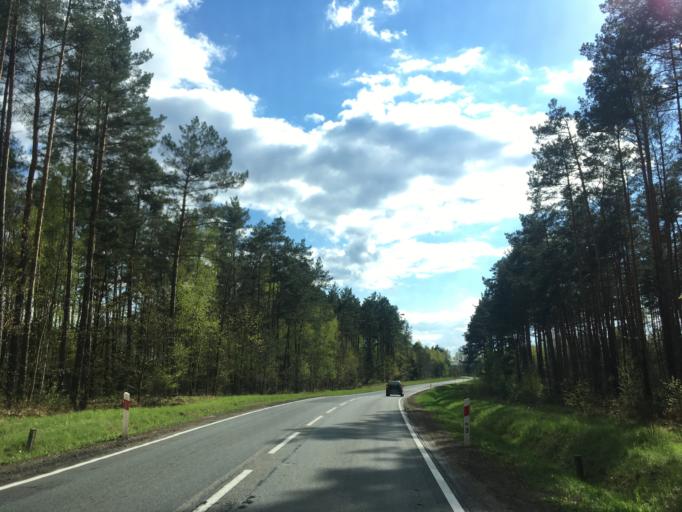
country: PL
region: Warmian-Masurian Voivodeship
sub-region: Powiat szczycienski
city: Pasym
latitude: 53.5534
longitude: 20.8625
